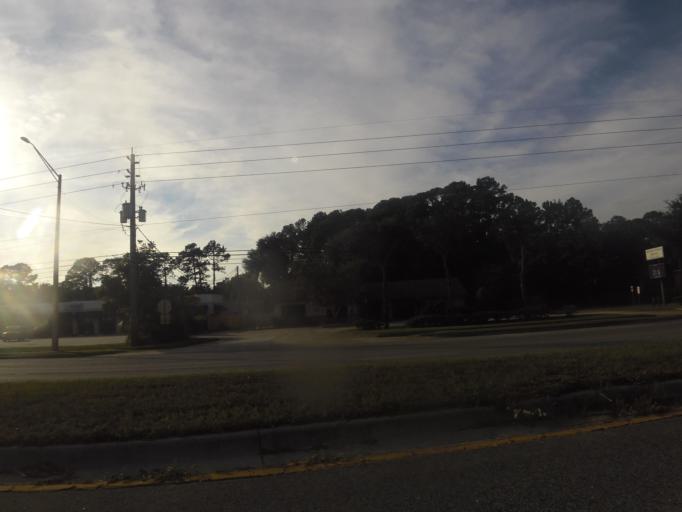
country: US
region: Florida
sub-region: Saint Johns County
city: Fruit Cove
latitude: 30.1957
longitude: -81.6231
